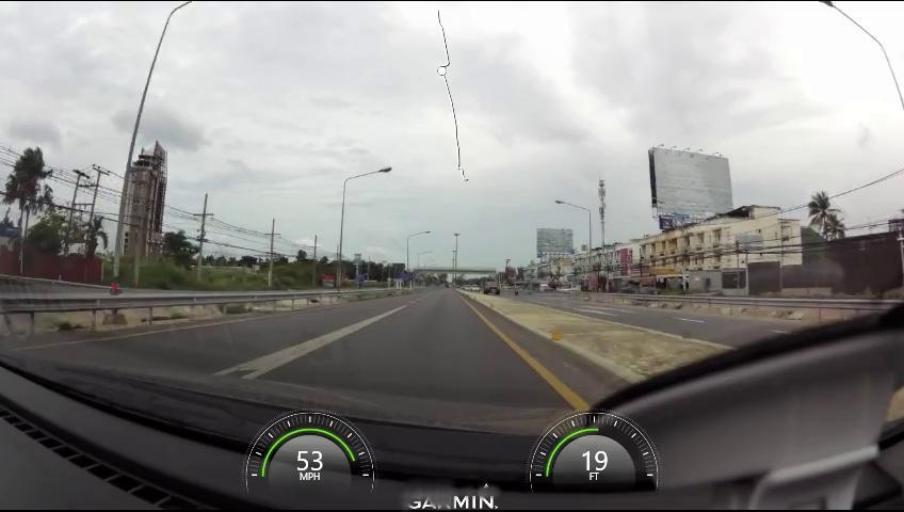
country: TH
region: Prachuap Khiri Khan
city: Hua Hin
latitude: 12.5343
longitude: 99.9602
